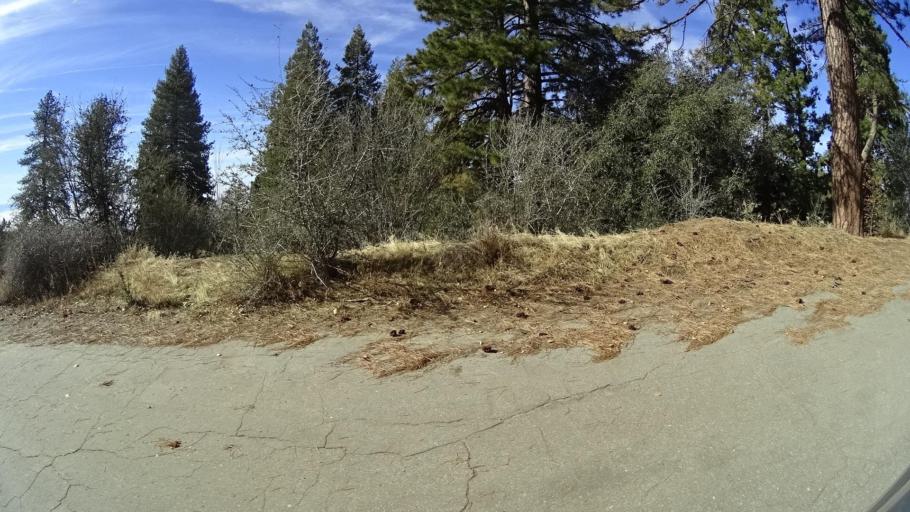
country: US
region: California
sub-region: Kern County
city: Bodfish
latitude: 35.4761
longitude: -118.6468
